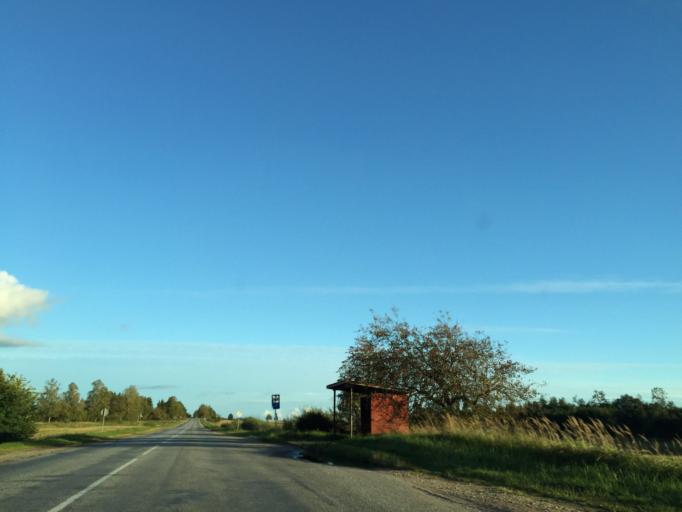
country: LV
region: Saldus Rajons
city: Saldus
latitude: 56.7255
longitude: 22.3817
